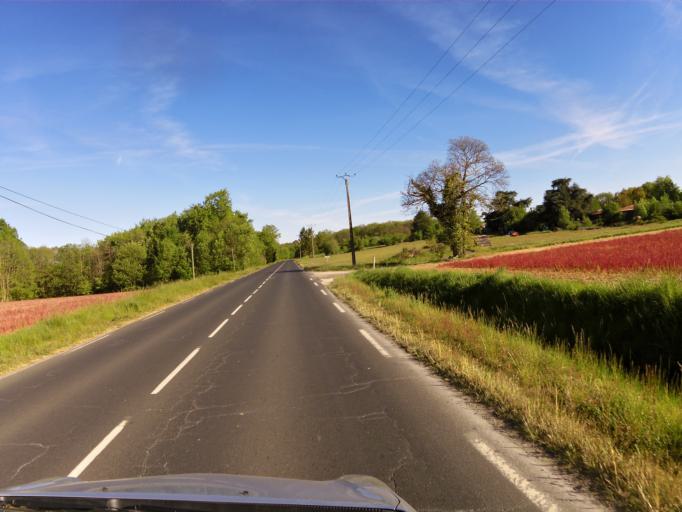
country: FR
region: Aquitaine
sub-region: Departement de la Dordogne
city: Montignac
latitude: 45.0156
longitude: 1.2374
